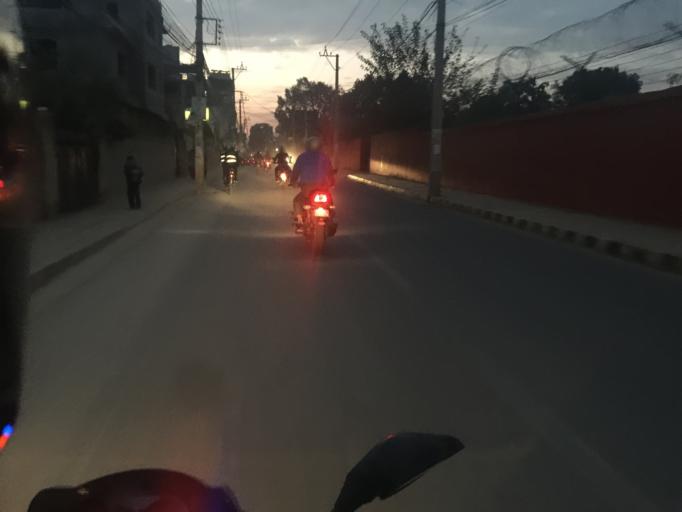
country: NP
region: Central Region
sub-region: Bagmati Zone
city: Patan
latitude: 27.6796
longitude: 85.3078
